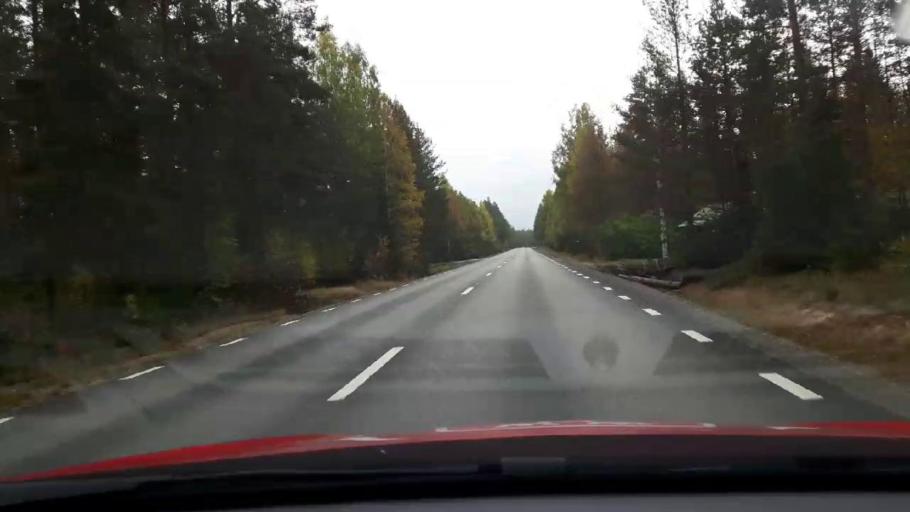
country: SE
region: Gaevleborg
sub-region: Ljusdals Kommun
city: Farila
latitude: 61.8565
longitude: 15.7458
